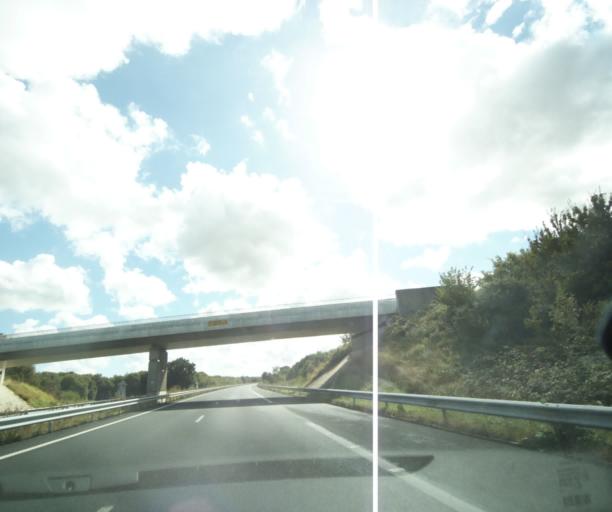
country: FR
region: Poitou-Charentes
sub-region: Departement de la Charente-Maritime
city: Bords
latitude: 45.9073
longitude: -0.7749
